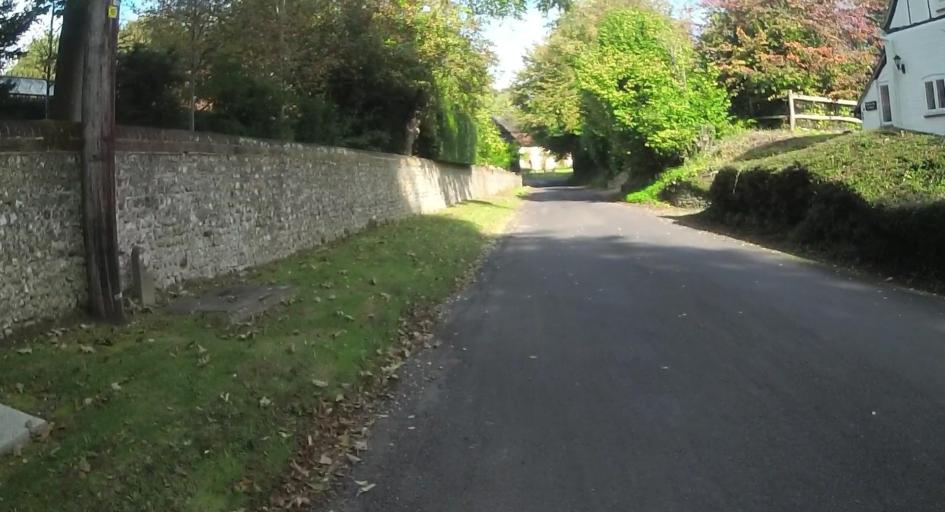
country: GB
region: England
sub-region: Hampshire
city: Alton
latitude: 51.1731
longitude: -1.0061
